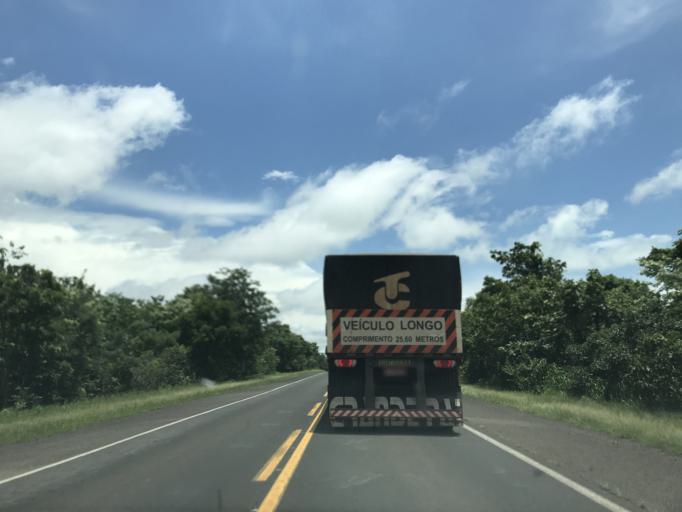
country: BR
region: Minas Gerais
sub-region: Prata
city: Prata
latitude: -19.6446
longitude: -48.9694
